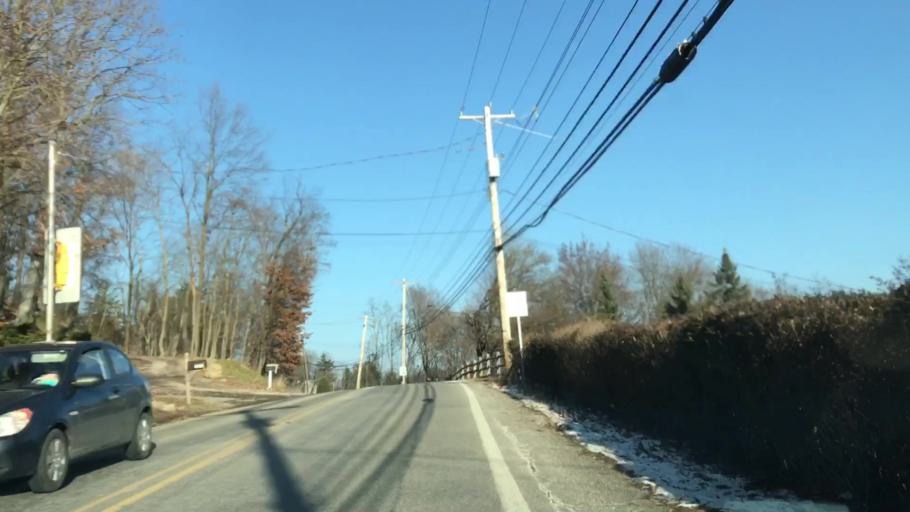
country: US
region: Pennsylvania
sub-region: Allegheny County
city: Allison Park
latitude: 40.5746
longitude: -80.0001
